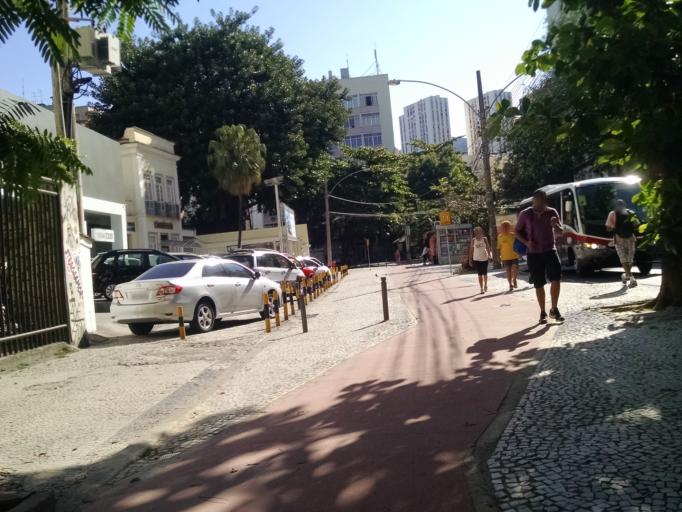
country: BR
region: Rio de Janeiro
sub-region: Rio De Janeiro
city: Rio de Janeiro
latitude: -22.9349
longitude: -43.1881
